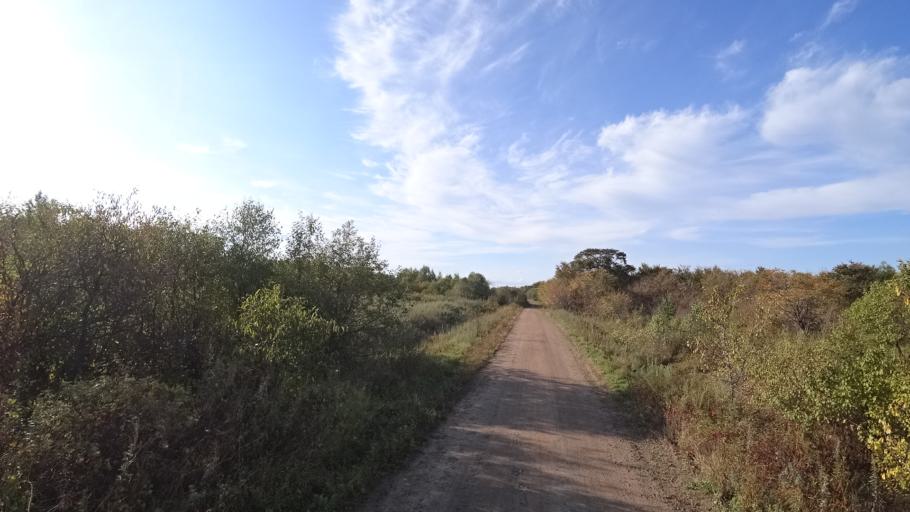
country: RU
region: Amur
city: Arkhara
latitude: 49.3487
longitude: 130.1161
